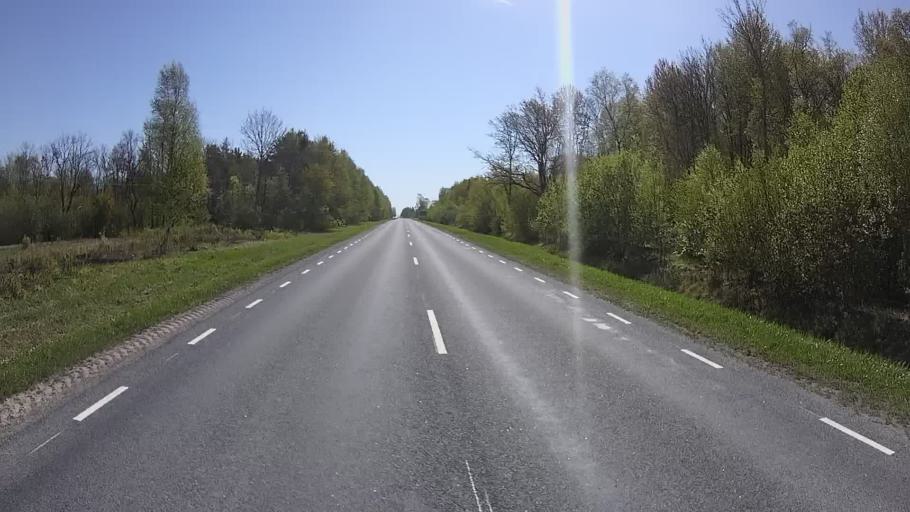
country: EE
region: Laeaene
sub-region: Lihula vald
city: Lihula
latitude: 58.5485
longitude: 23.9920
